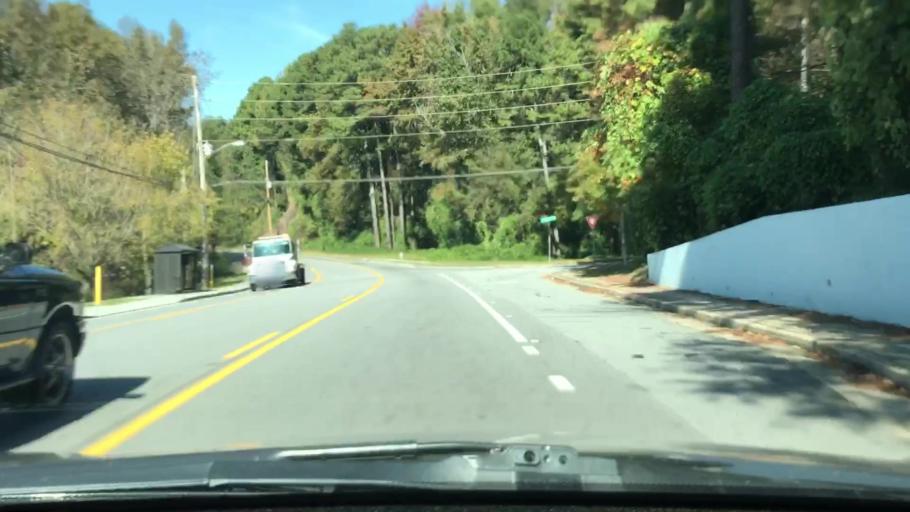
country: US
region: Georgia
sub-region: Gwinnett County
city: Norcross
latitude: 33.9282
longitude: -84.1958
